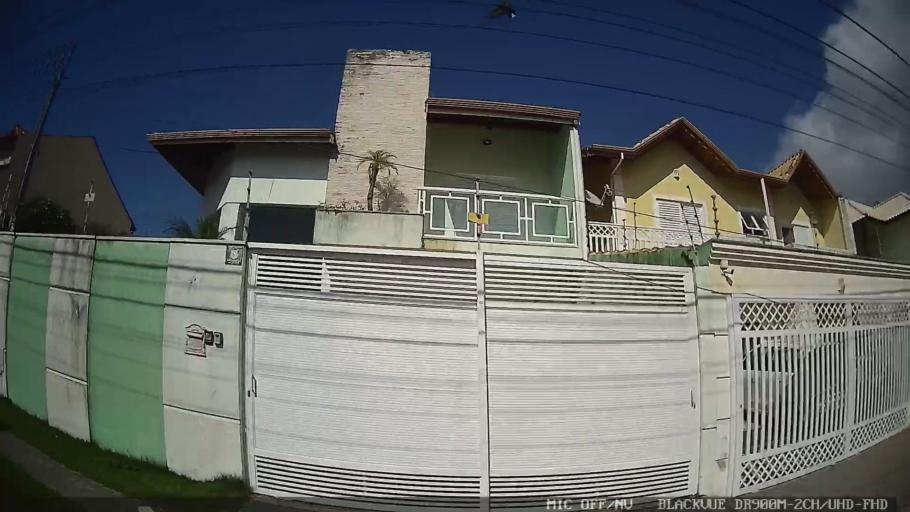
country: BR
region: Sao Paulo
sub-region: Peruibe
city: Peruibe
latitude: -24.2871
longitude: -46.9525
